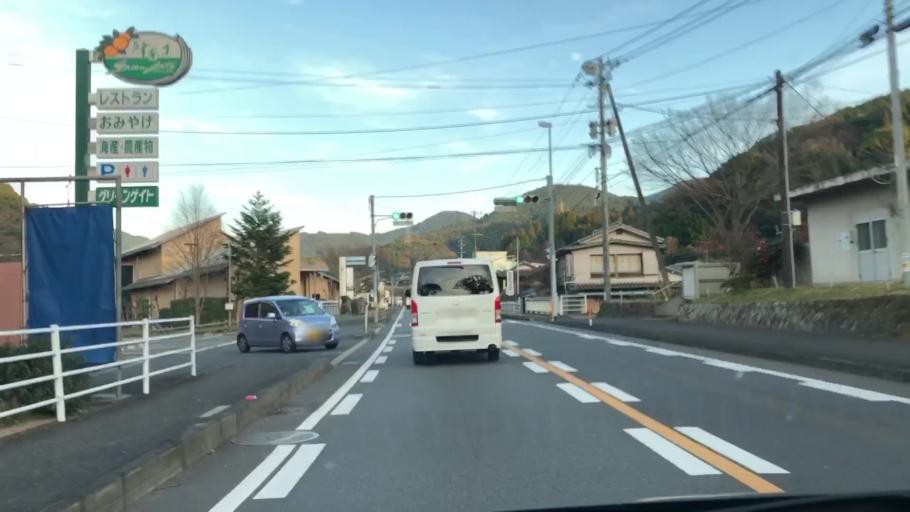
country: JP
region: Kumamoto
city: Minamata
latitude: 32.2315
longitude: 130.4569
